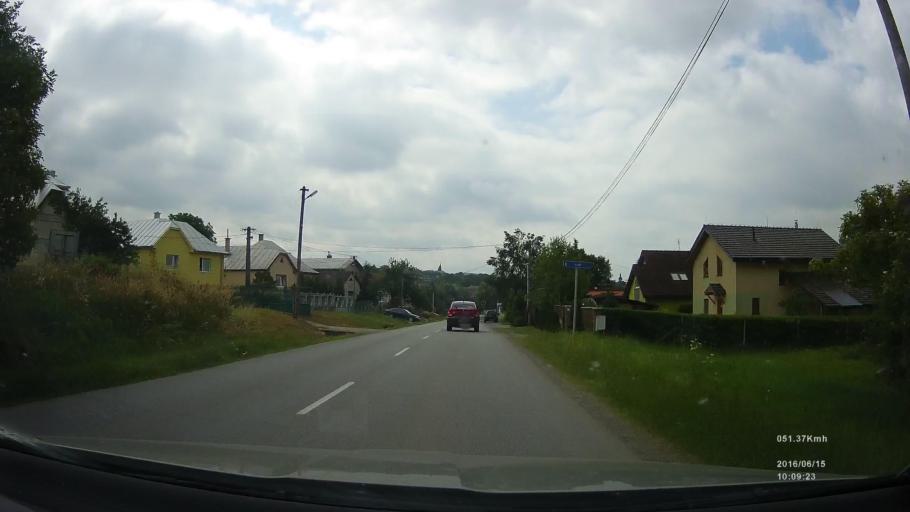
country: SK
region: Kosicky
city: Kosice
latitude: 48.7593
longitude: 21.3397
